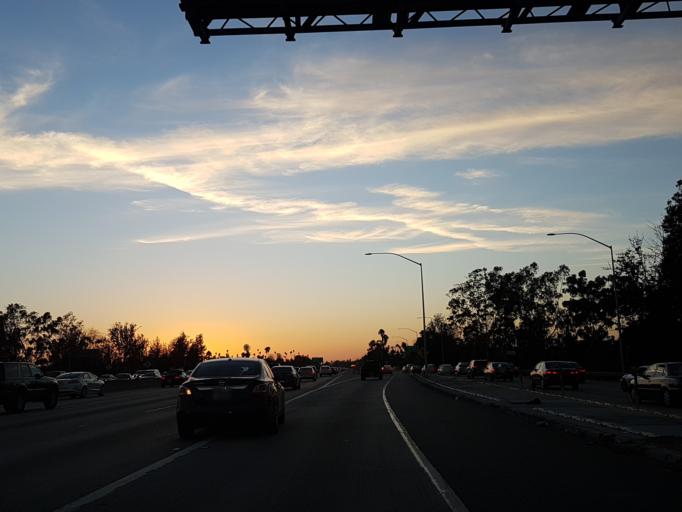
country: US
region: California
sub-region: Los Angeles County
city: Echo Park
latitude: 34.0372
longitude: -118.2948
